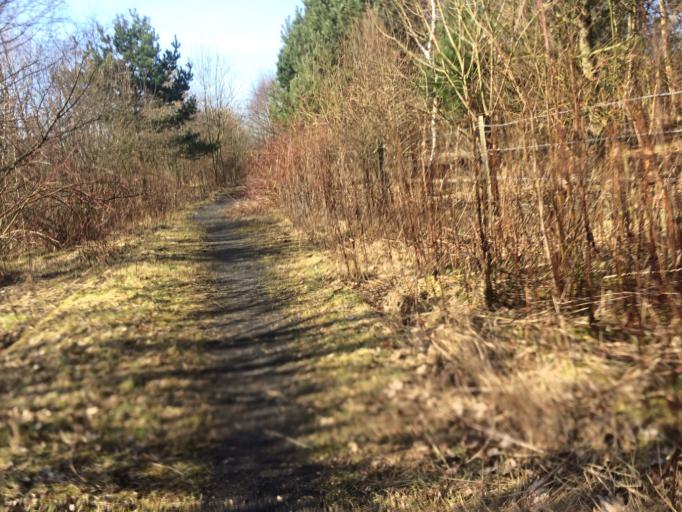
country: GB
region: Scotland
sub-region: Fife
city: Kirkcaldy
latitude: 56.1354
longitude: -3.2028
